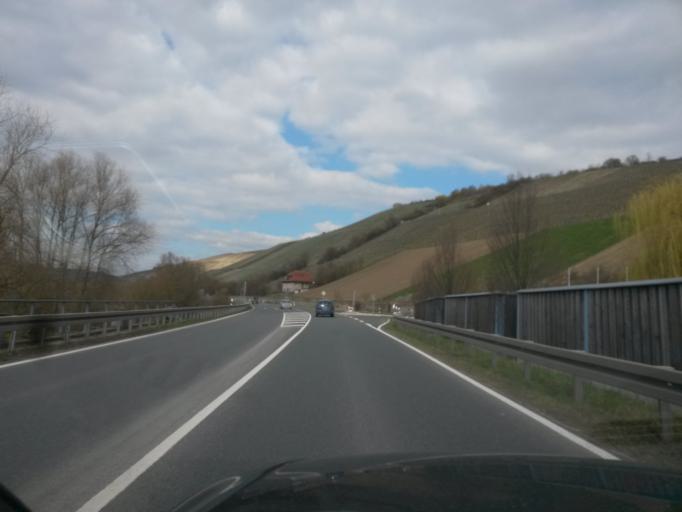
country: DE
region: Bavaria
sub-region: Regierungsbezirk Unterfranken
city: Randersacker
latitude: 49.7605
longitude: 9.9770
